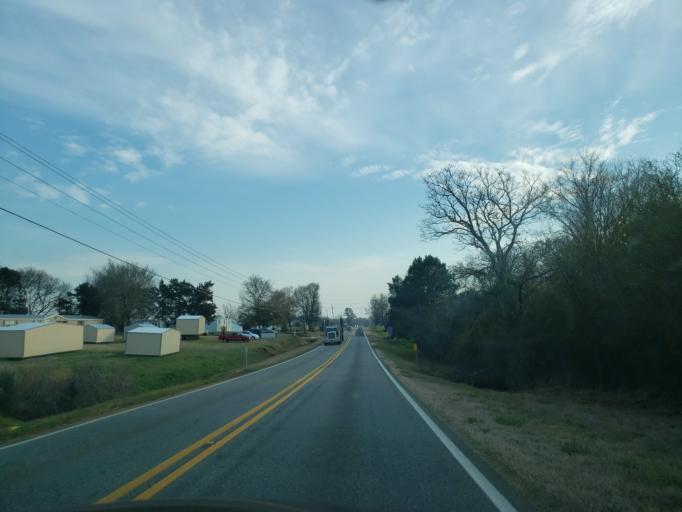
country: US
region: Alabama
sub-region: Hale County
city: Moundville
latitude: 32.9765
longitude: -87.6245
